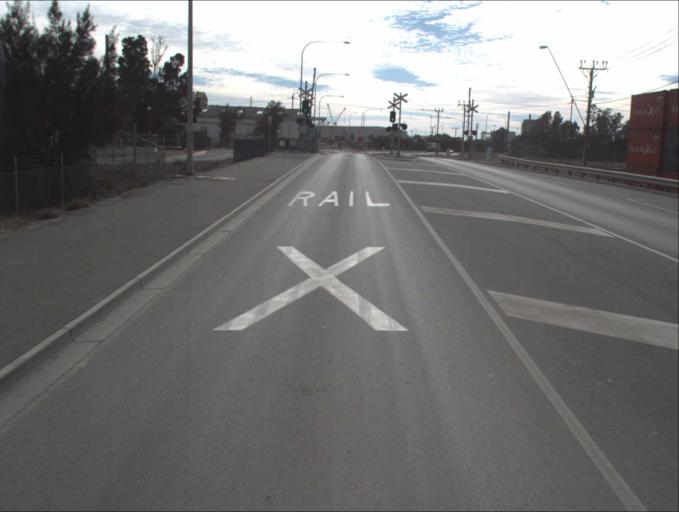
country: AU
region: South Australia
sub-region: Port Adelaide Enfield
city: Birkenhead
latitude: -34.8382
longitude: 138.5147
